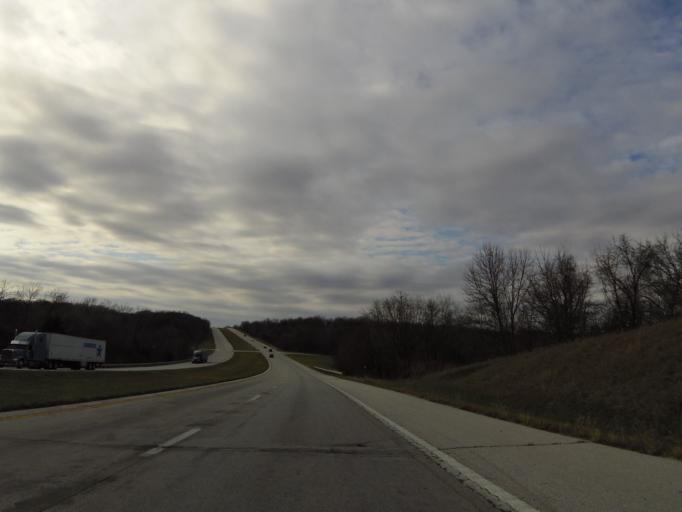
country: US
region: Missouri
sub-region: Marion County
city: Hannibal
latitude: 39.7437
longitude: -91.4266
